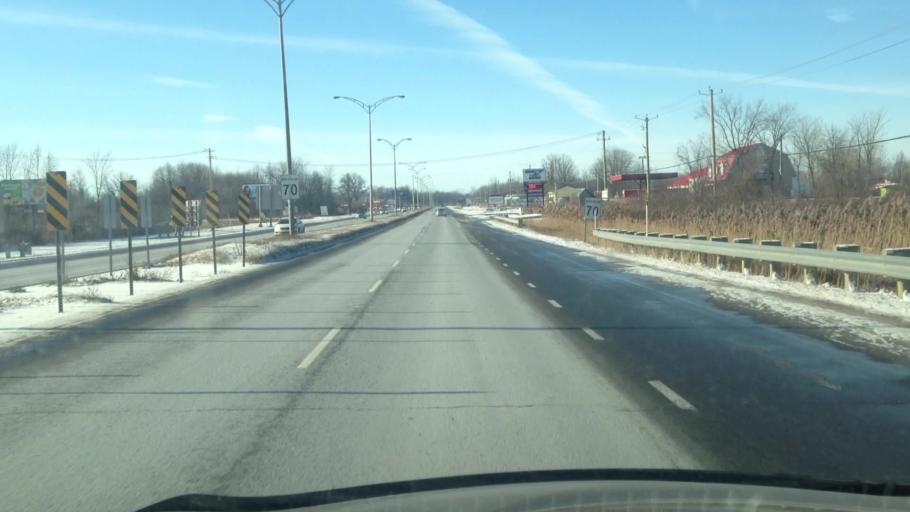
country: CA
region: Quebec
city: Montreal-Ouest
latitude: 45.4022
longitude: -73.6740
